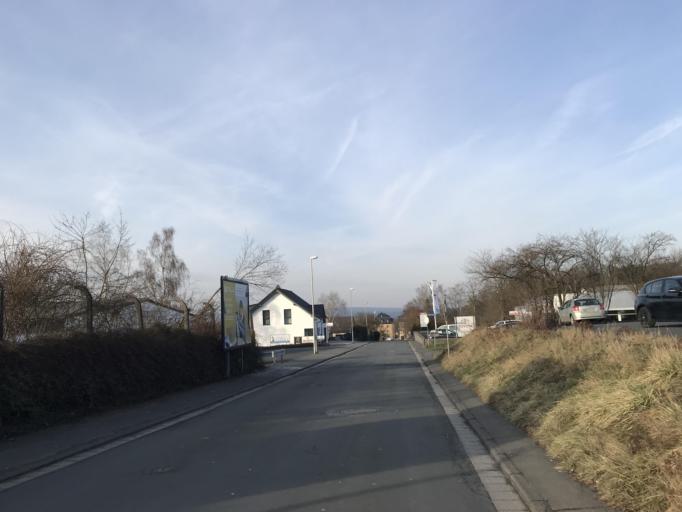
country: DE
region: Hesse
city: Weilburg
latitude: 50.4831
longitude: 8.2847
